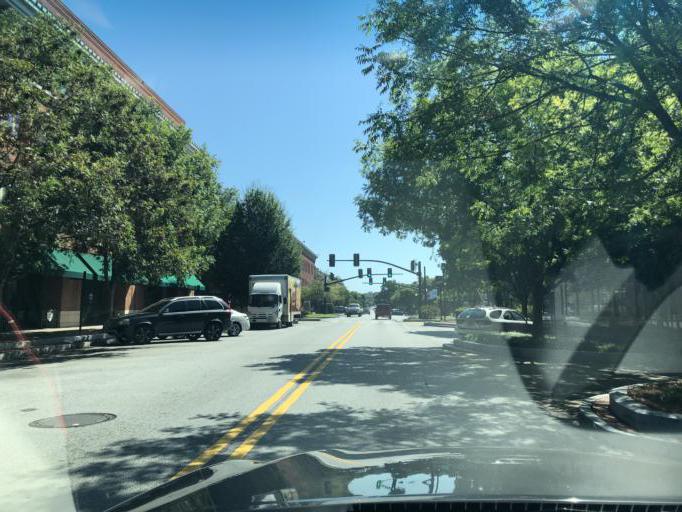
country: US
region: Georgia
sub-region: Muscogee County
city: Columbus
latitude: 32.4646
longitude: -84.9948
